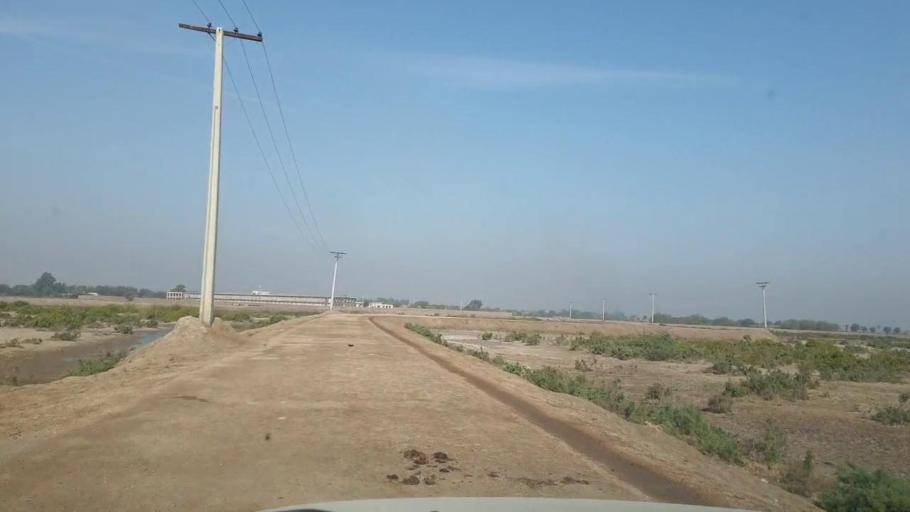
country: PK
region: Sindh
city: Mirpur Khas
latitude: 25.5070
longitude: 69.0466
